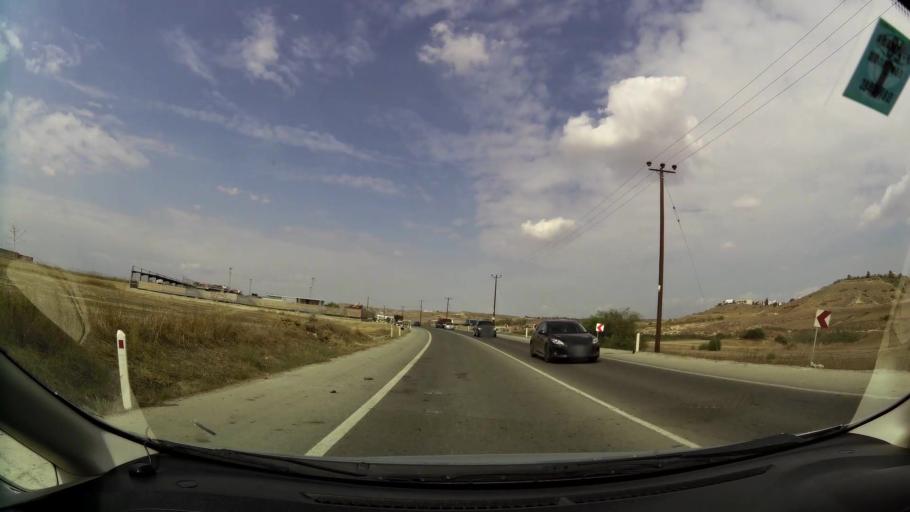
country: CY
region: Lefkosia
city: Tseri
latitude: 35.0571
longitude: 33.3722
